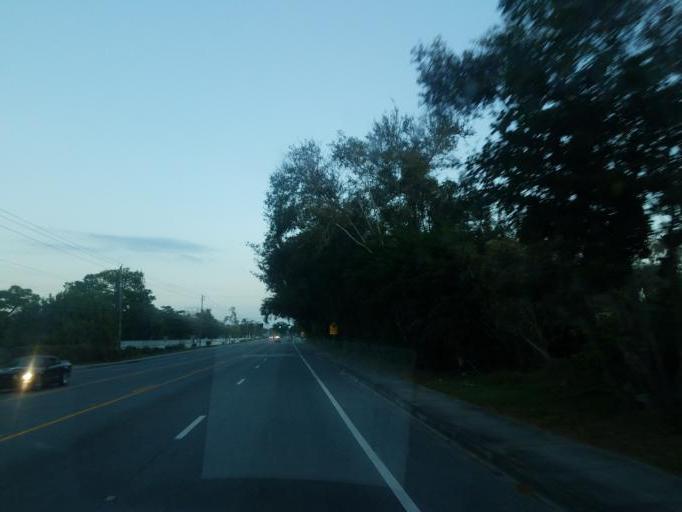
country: US
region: Florida
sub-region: Sarasota County
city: Kensington Park
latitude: 27.3614
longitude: -82.5056
